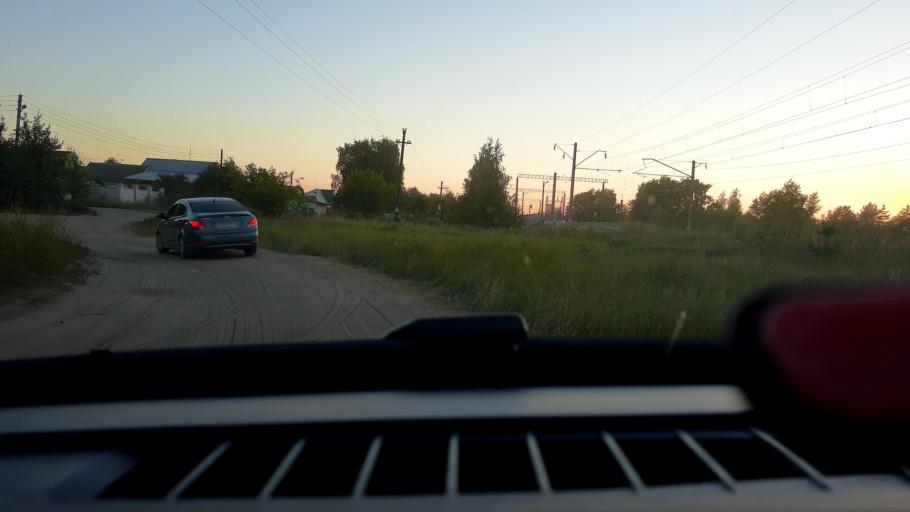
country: RU
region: Nizjnij Novgorod
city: Gorbatovka
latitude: 56.3823
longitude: 43.7654
